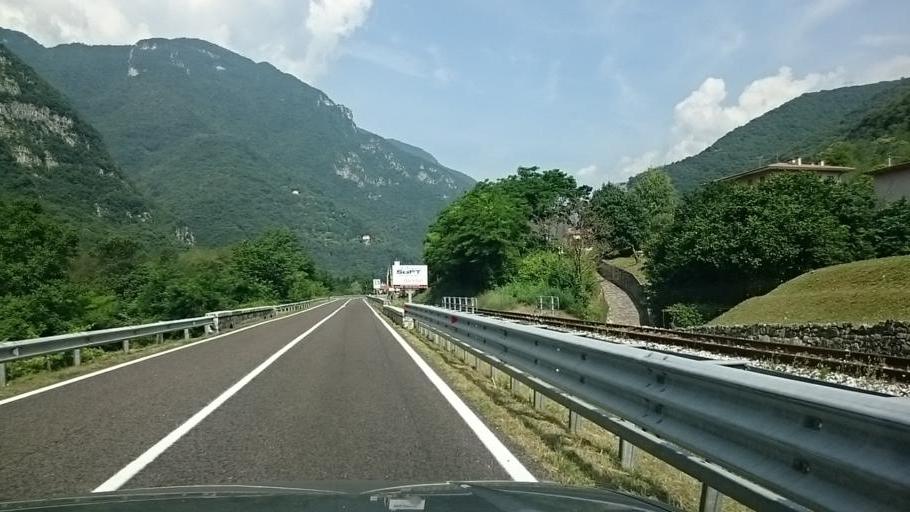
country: IT
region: Veneto
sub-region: Provincia di Vicenza
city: San Nazario
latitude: 45.8417
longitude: 11.6838
